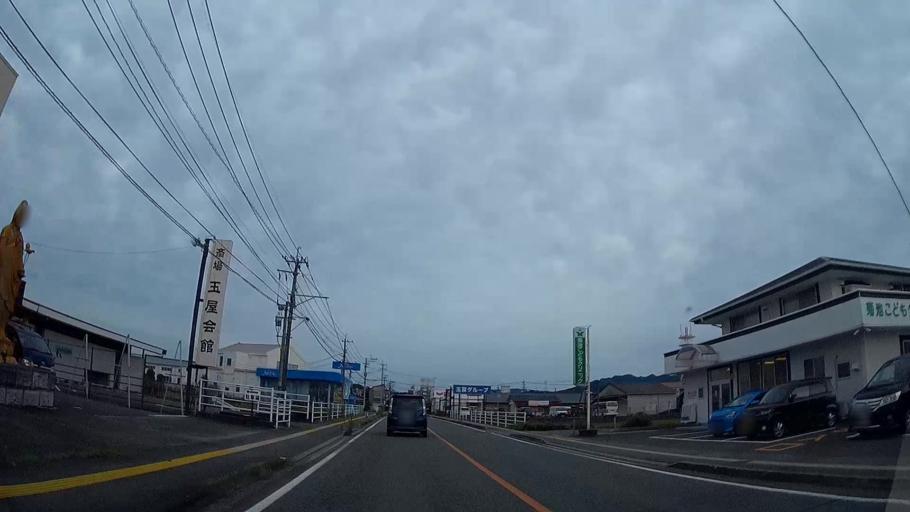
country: JP
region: Kumamoto
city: Kikuchi
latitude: 32.9757
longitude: 130.8079
